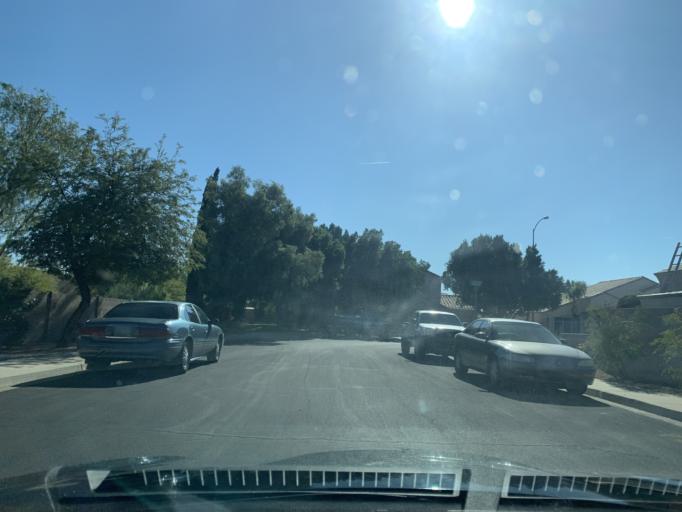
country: US
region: Arizona
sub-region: Pinal County
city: Apache Junction
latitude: 33.3854
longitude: -111.6178
